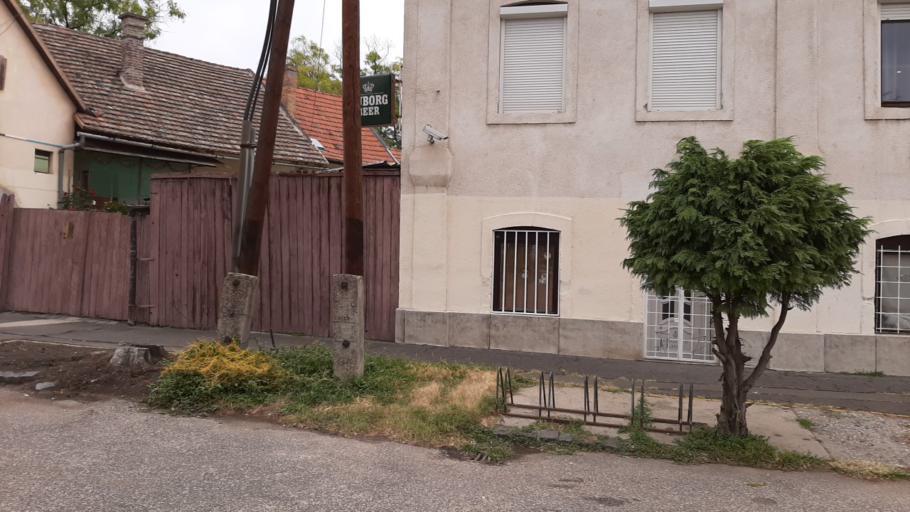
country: HU
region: Csongrad
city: Szeged
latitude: 46.2431
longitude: 20.1321
